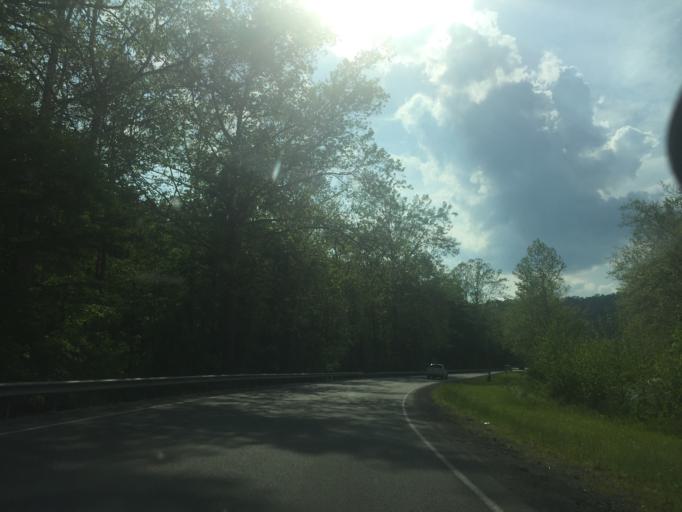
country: US
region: West Virginia
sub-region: Tucker County
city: Parsons
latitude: 38.9524
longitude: -79.5026
